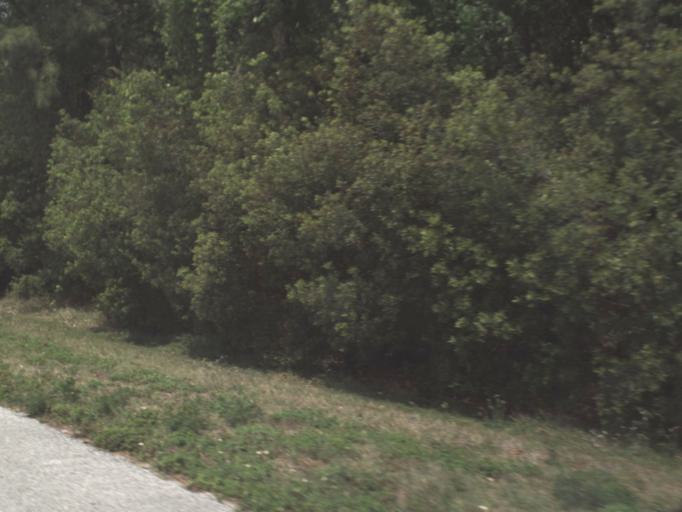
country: US
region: Florida
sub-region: Lake County
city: Mount Plymouth
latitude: 28.8604
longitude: -81.5130
